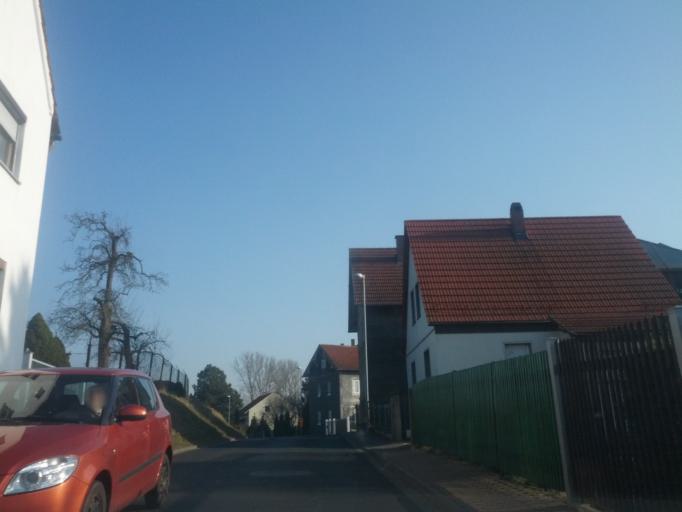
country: DE
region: Thuringia
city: Bischofroda
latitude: 51.0418
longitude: 10.3888
